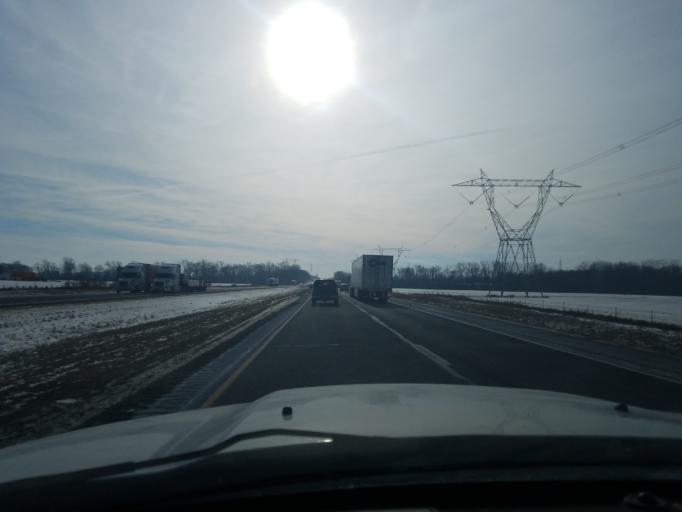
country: US
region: Indiana
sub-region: Huntington County
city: Roanoke
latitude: 40.9240
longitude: -85.3198
